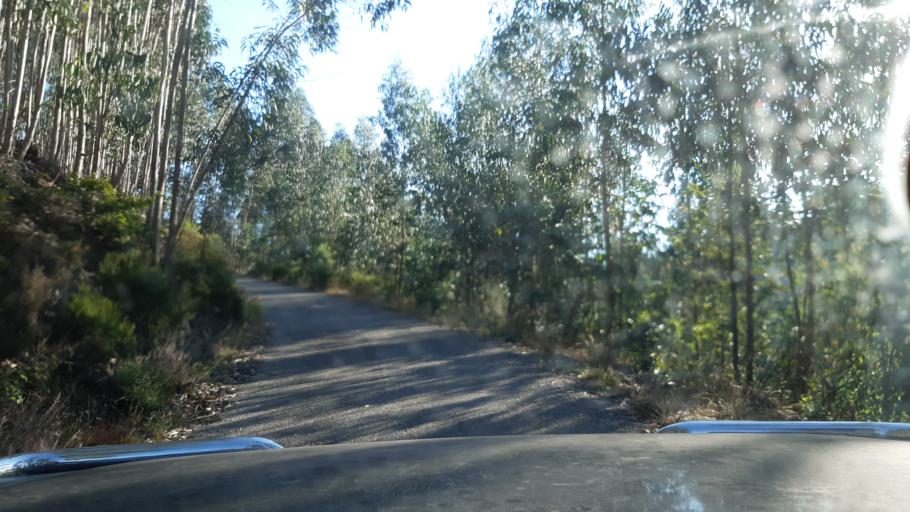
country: PT
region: Viseu
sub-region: Mortagua
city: Mortagua
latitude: 40.5280
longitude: -8.2556
